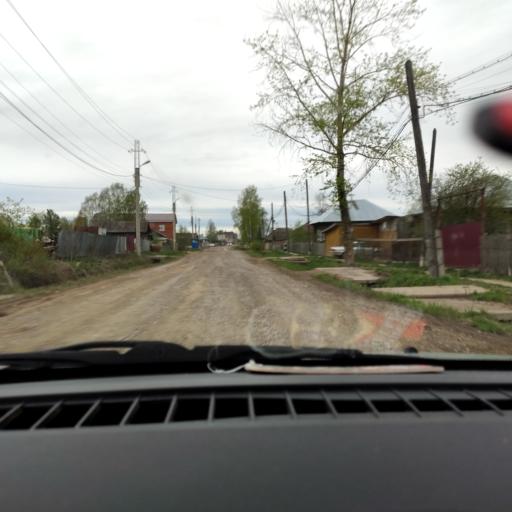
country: RU
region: Perm
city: Kudymkar
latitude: 59.0105
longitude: 54.6383
